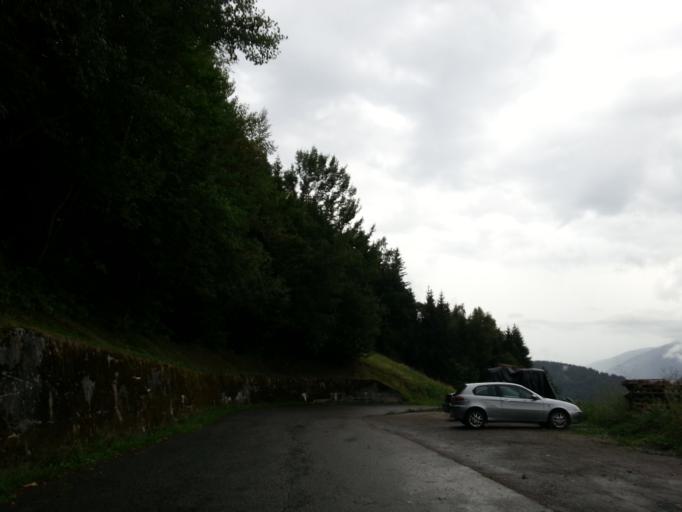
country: FR
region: Rhone-Alpes
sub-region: Departement de la Savoie
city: Marthod
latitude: 45.7080
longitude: 6.4615
